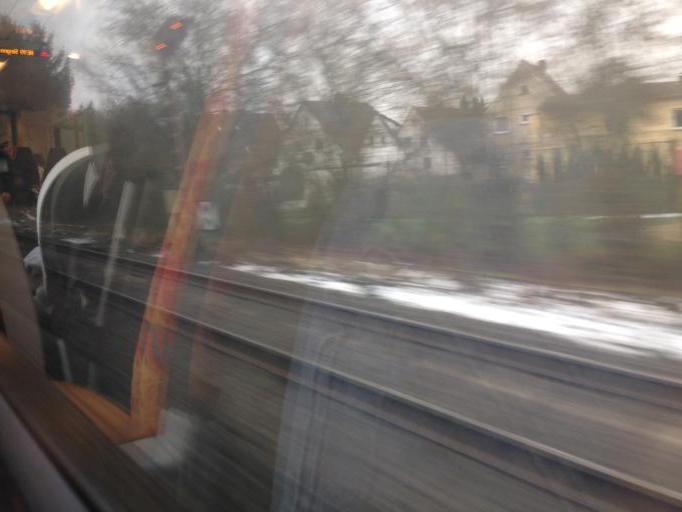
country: DE
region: Hesse
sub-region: Regierungsbezirk Giessen
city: Asslar
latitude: 50.5847
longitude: 8.4733
